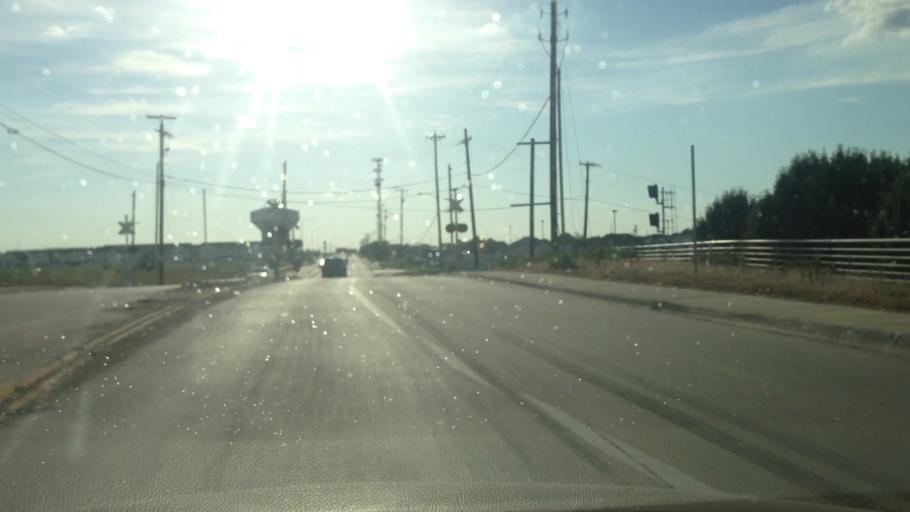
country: US
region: Texas
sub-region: Tarrant County
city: Haslet
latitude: 32.9689
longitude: -97.4034
